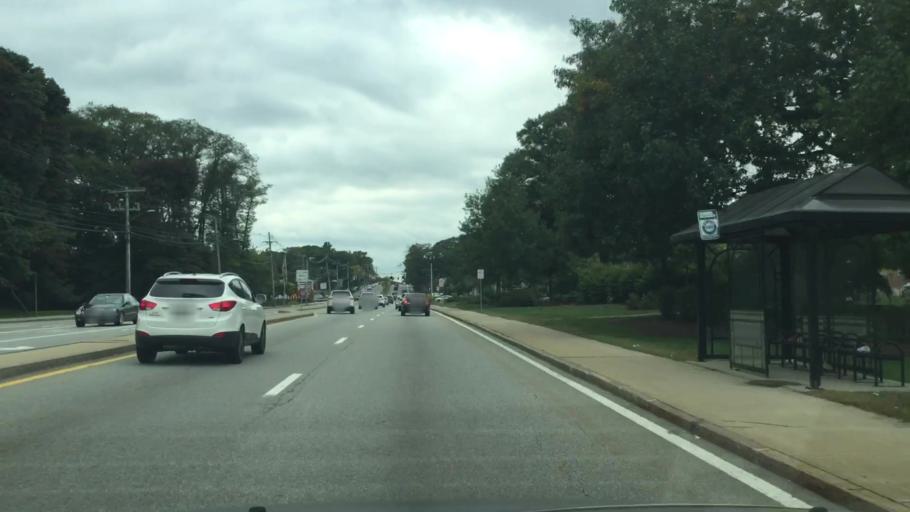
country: US
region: Massachusetts
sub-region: Middlesex County
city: Framingham
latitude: 42.3041
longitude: -71.3991
